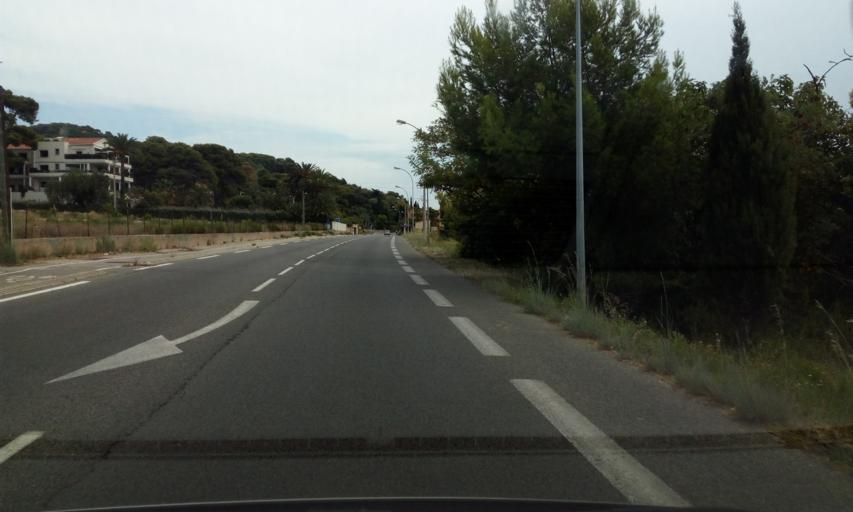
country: FR
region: Provence-Alpes-Cote d'Azur
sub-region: Departement du Var
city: Carqueiranne
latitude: 43.0895
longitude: 6.0884
